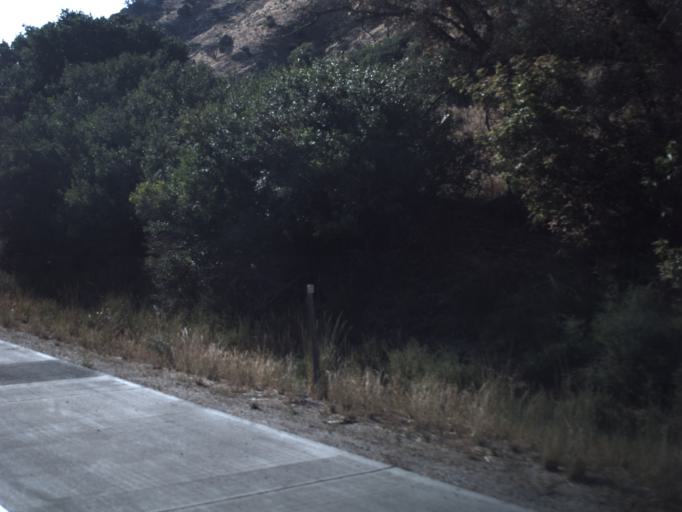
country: US
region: Utah
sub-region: Morgan County
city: Morgan
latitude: 41.0639
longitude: -111.5605
